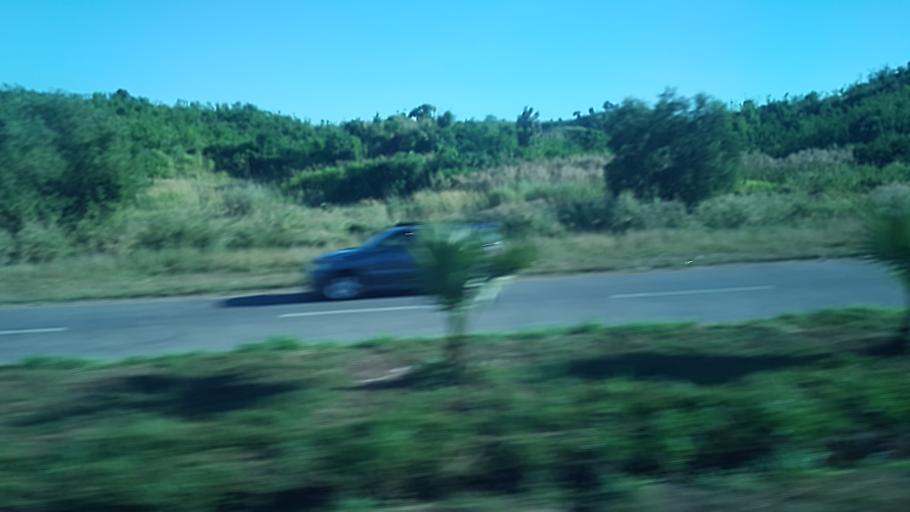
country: MM
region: Bago
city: Nyaunglebin
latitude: 17.6983
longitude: 96.4745
